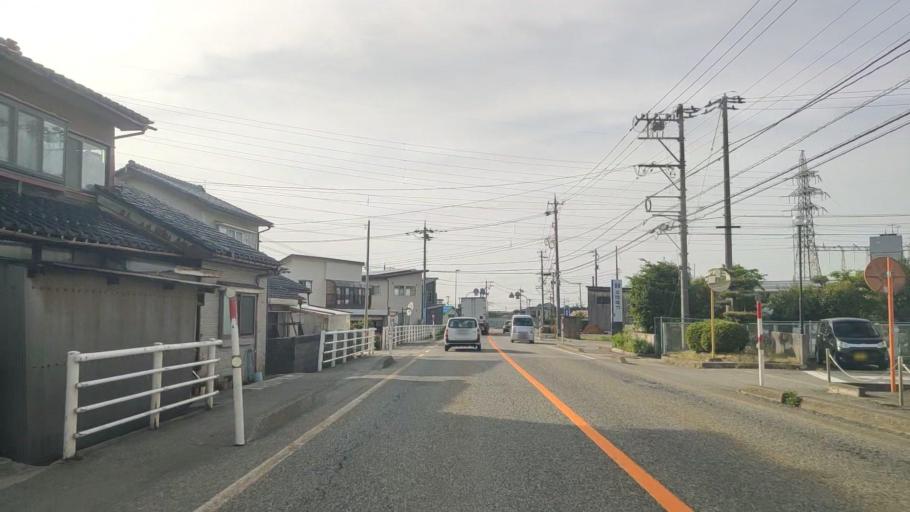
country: JP
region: Toyama
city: Yatsuomachi-higashikumisaka
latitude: 36.5654
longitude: 137.2117
